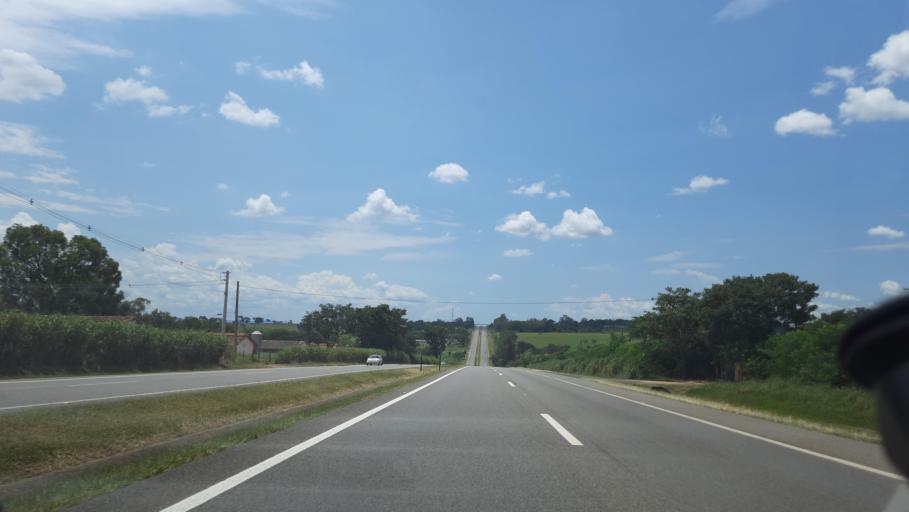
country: BR
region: Sao Paulo
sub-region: Mococa
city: Mococa
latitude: -21.5934
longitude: -47.0398
